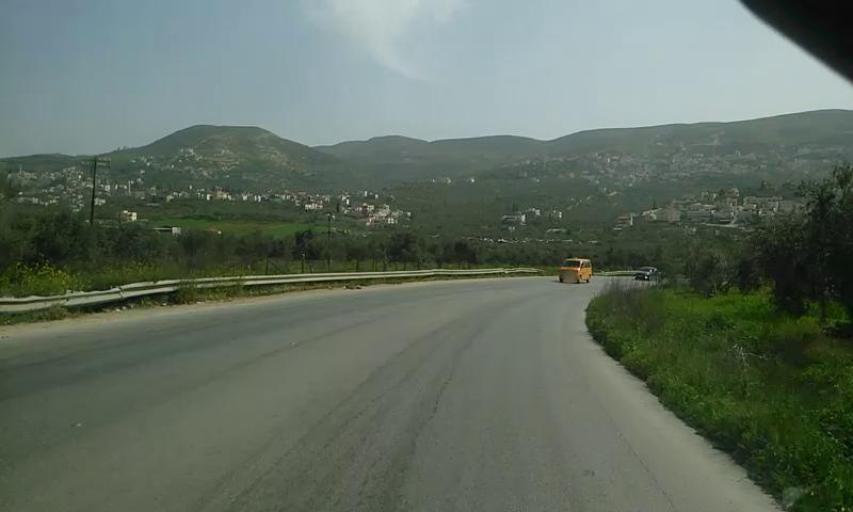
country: PS
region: West Bank
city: Al Fandaqumiyah
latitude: 32.3367
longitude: 35.2065
